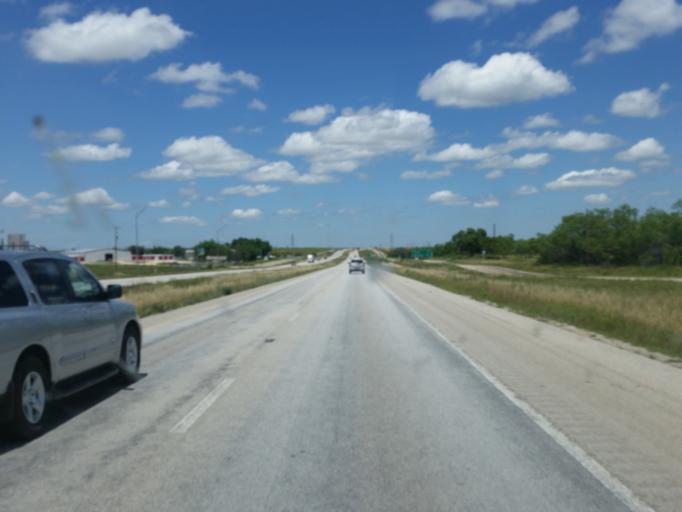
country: US
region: Texas
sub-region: Nolan County
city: Sweetwater
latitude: 32.4566
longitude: -100.3882
